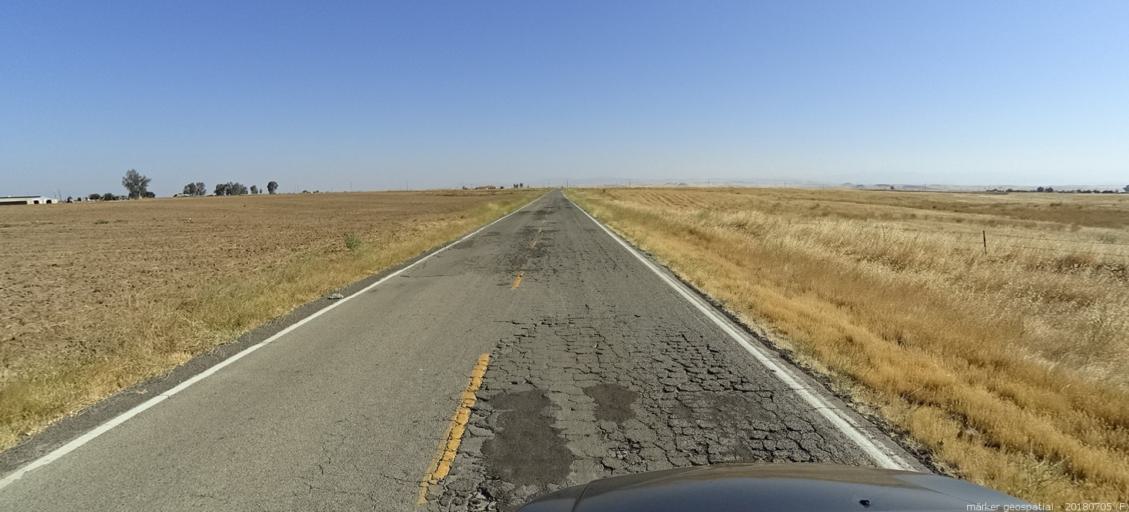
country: US
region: California
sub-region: Madera County
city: Madera Acres
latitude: 37.1184
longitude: -120.0746
